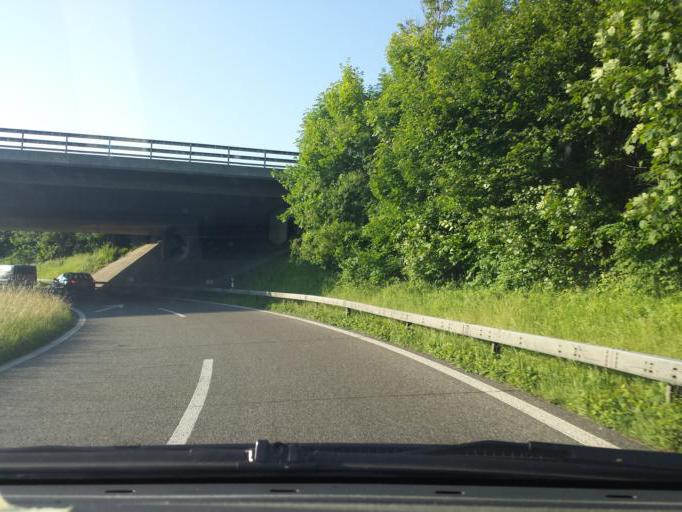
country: CH
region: Saint Gallen
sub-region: Wahlkreis Rorschach
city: Morschwil
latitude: 47.4689
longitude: 9.4429
